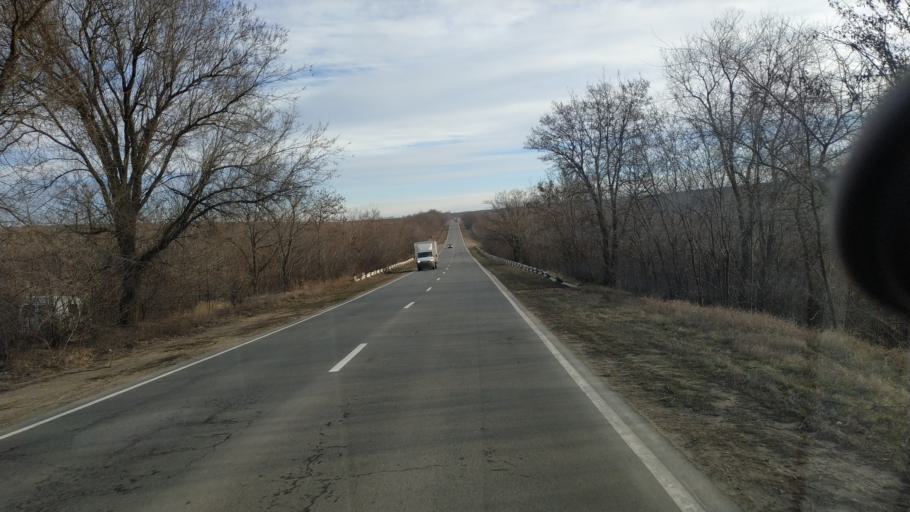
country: MD
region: Chisinau
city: Vadul lui Voda
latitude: 47.0808
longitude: 29.0342
